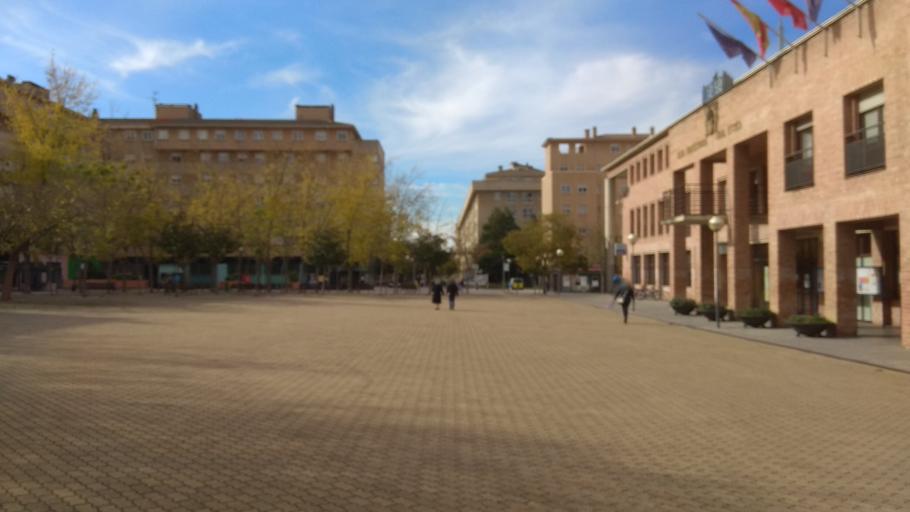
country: ES
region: Navarre
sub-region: Provincia de Navarra
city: Baranain
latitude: 42.8047
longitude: -1.6839
